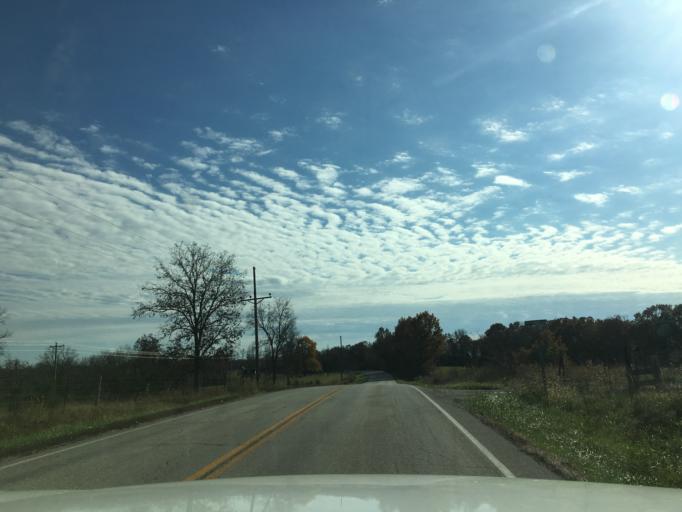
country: US
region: Missouri
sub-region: Maries County
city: Belle
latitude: 38.3655
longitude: -91.8090
